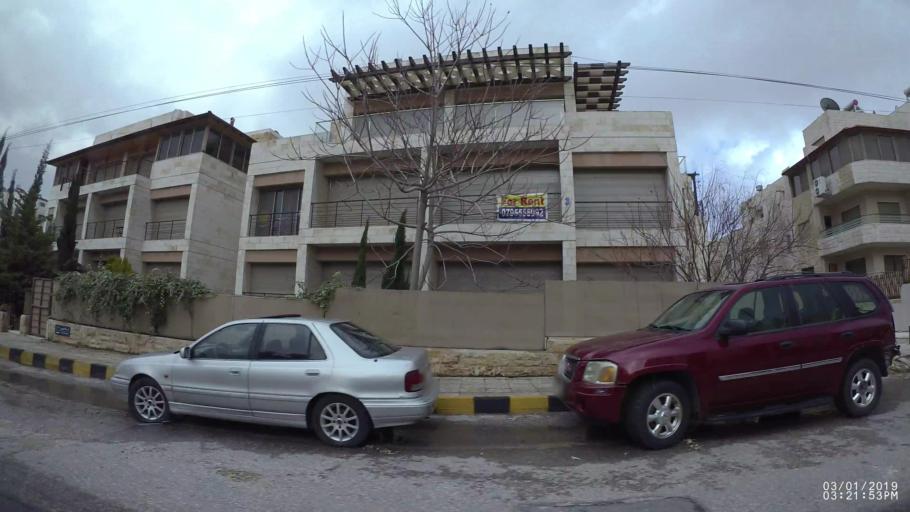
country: JO
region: Amman
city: Al Bunayyat ash Shamaliyah
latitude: 31.9480
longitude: 35.8829
